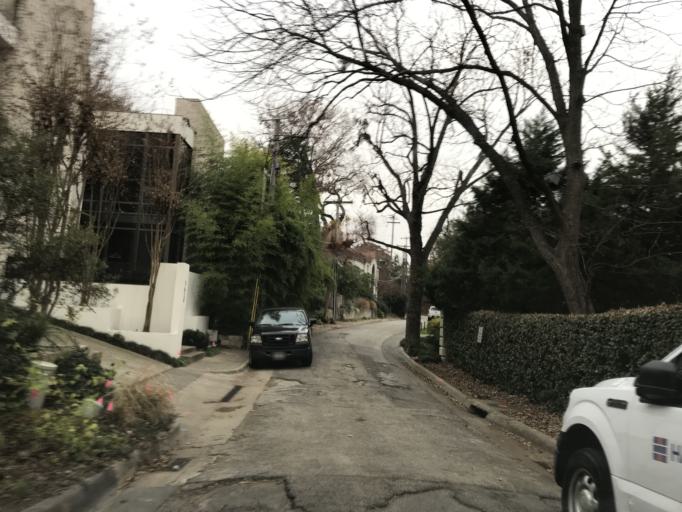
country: US
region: Texas
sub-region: Dallas County
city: Highland Park
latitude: 32.8128
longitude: -96.7986
